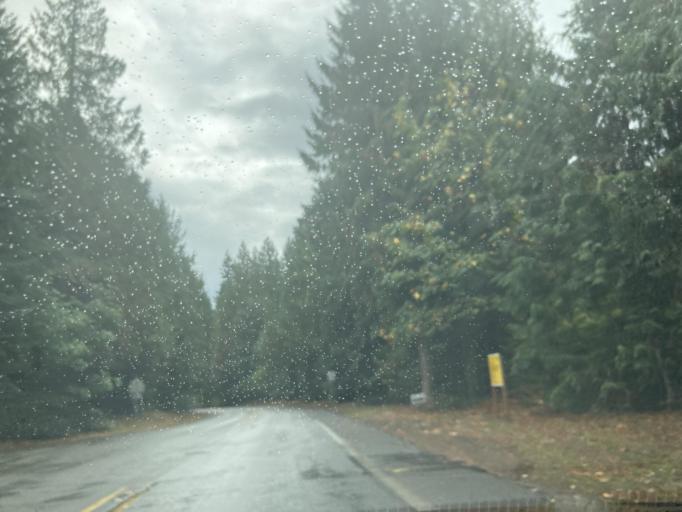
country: US
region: Washington
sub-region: Pierce County
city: South Hill
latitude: 47.1582
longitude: -122.2684
